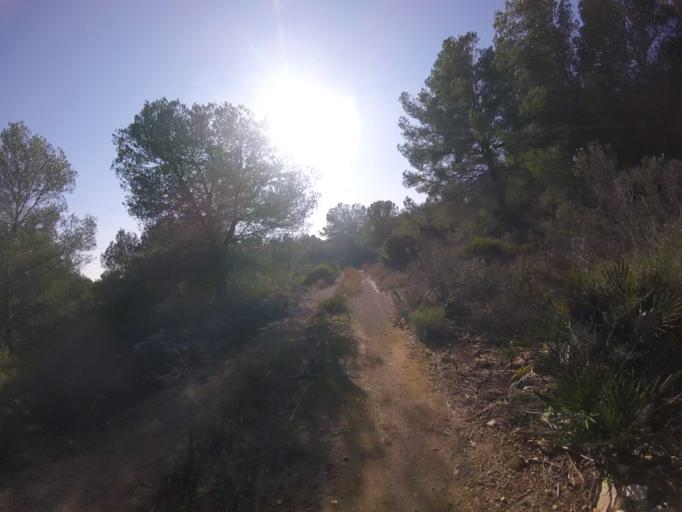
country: ES
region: Valencia
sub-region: Provincia de Castello
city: Santa Magdalena de Pulpis
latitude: 40.3037
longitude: 0.3335
